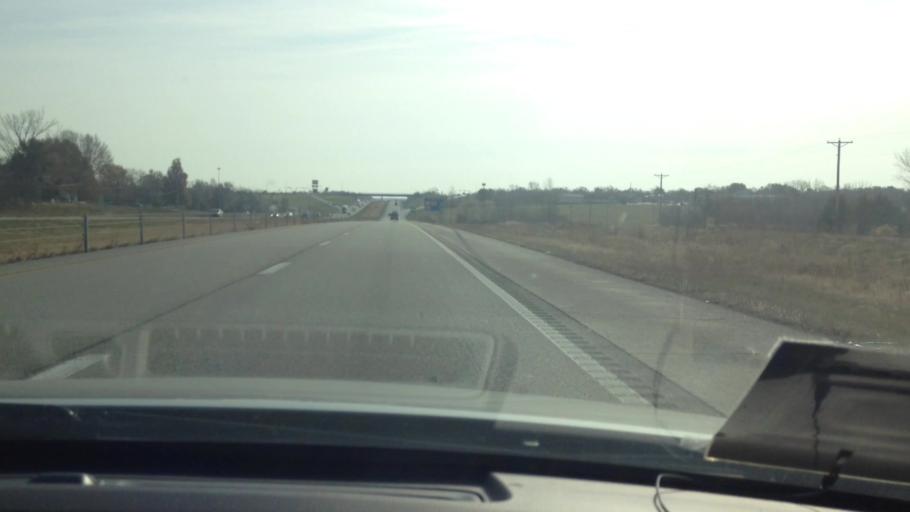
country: US
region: Missouri
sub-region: Cass County
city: Peculiar
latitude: 38.7300
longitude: -94.4616
